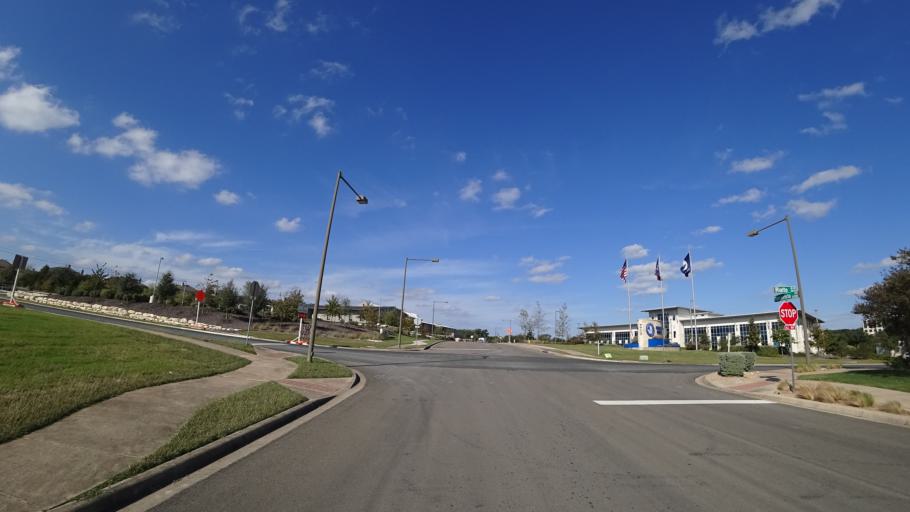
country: US
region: Texas
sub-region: Travis County
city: Barton Creek
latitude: 30.2534
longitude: -97.8772
